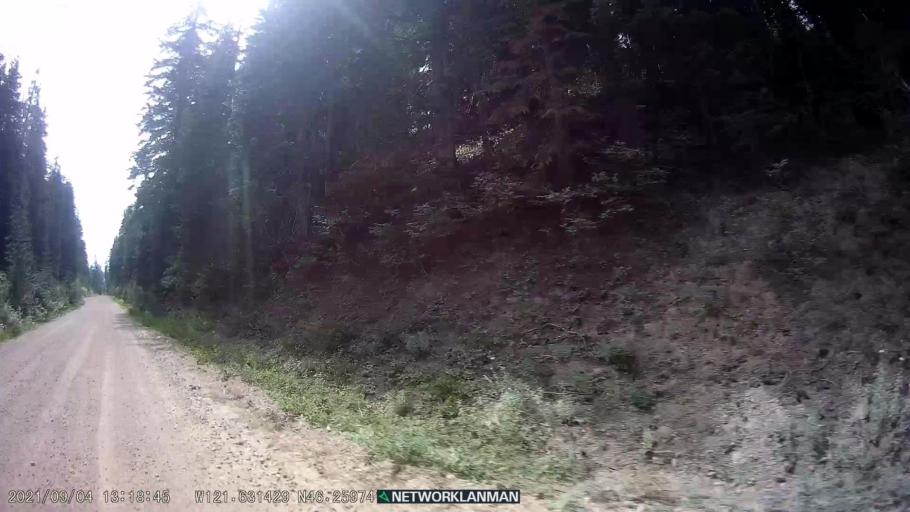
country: US
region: Washington
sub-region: Klickitat County
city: White Salmon
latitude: 46.2596
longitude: -121.6314
